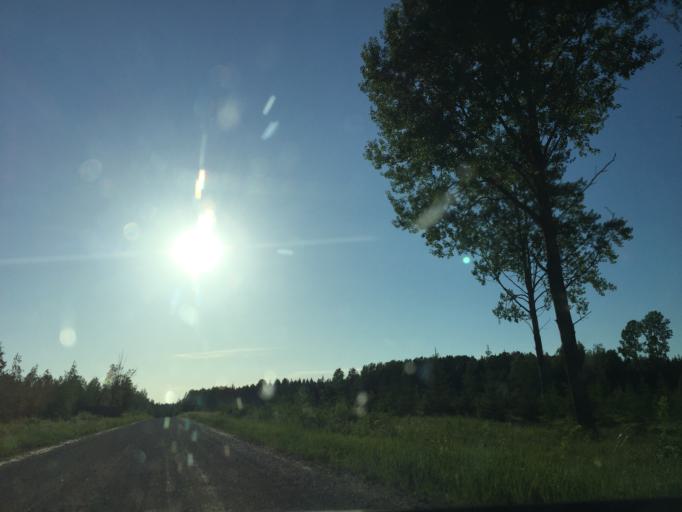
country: LV
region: Talsu Rajons
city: Sabile
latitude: 56.8642
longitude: 22.6527
